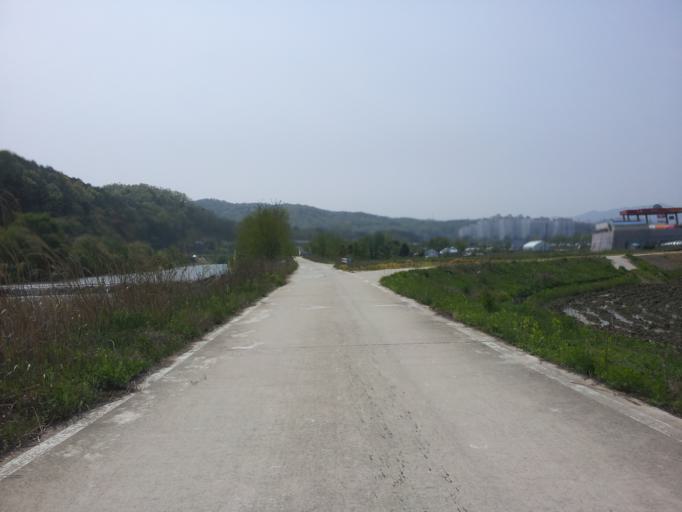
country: KR
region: Daejeon
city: Daejeon
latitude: 36.2659
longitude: 127.2865
